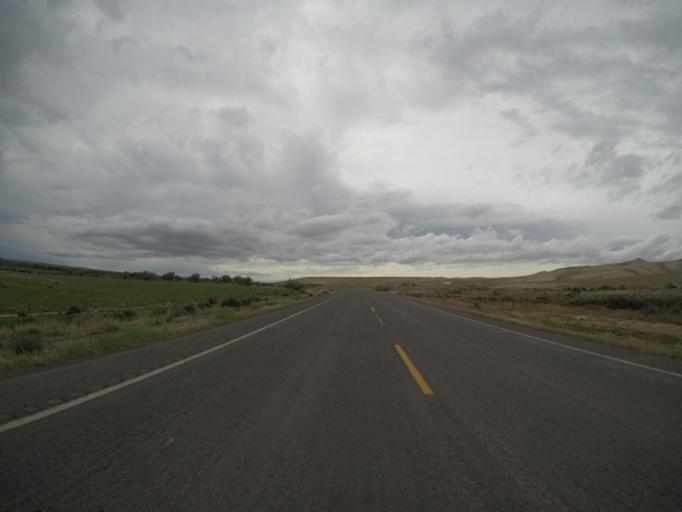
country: US
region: Wyoming
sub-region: Big Horn County
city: Lovell
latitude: 44.8770
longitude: -108.3031
